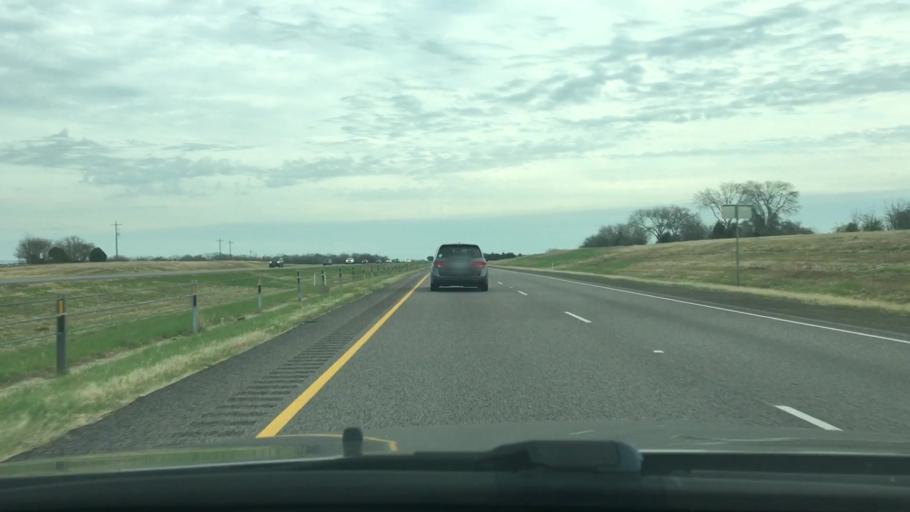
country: US
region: Texas
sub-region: Madison County
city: Madisonville
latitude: 30.9508
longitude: -95.8622
